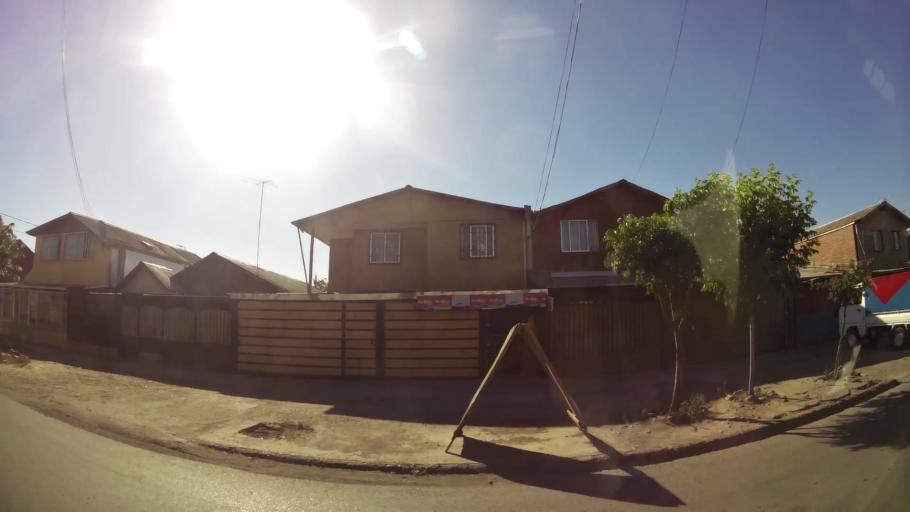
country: CL
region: Santiago Metropolitan
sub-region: Provincia de Maipo
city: San Bernardo
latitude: -33.5872
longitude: -70.6814
